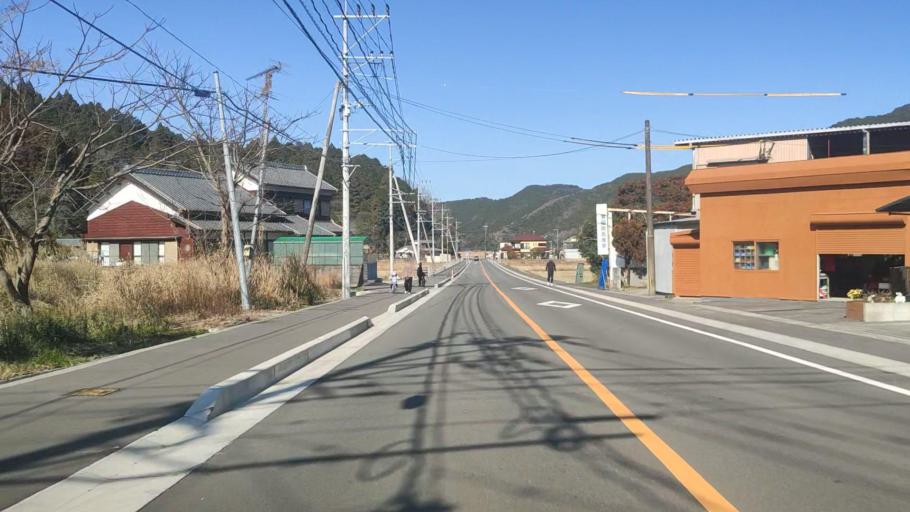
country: JP
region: Oita
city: Saiki
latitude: 32.9212
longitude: 131.9270
